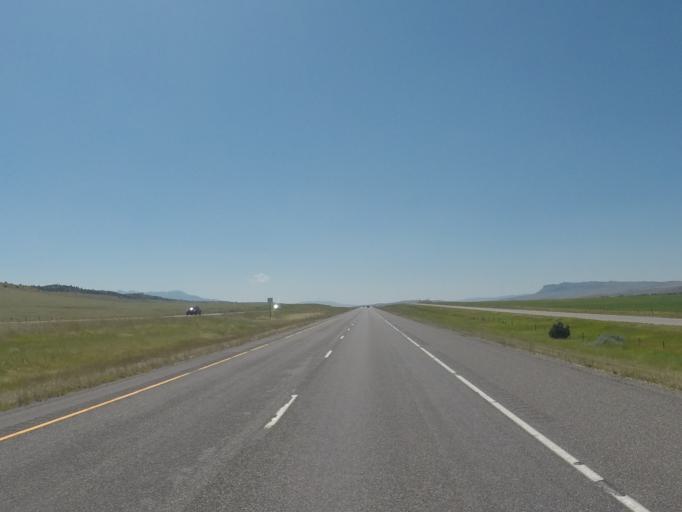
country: US
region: Montana
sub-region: Sweet Grass County
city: Big Timber
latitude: 45.7615
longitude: -110.1106
